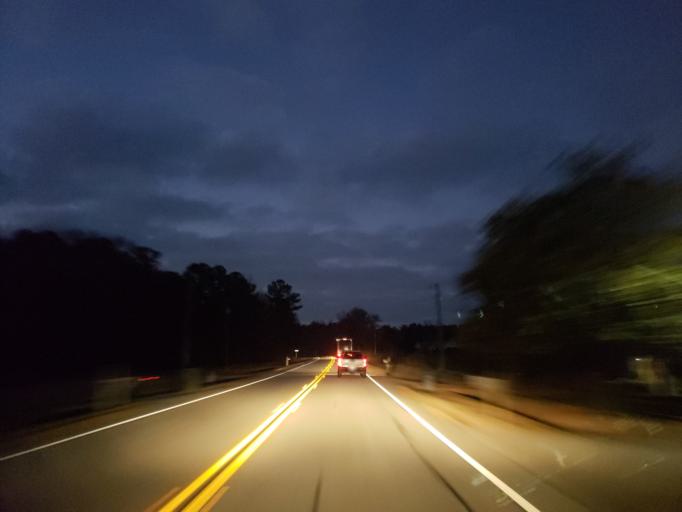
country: US
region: Georgia
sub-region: Polk County
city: Rockmart
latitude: 33.9389
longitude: -84.9973
